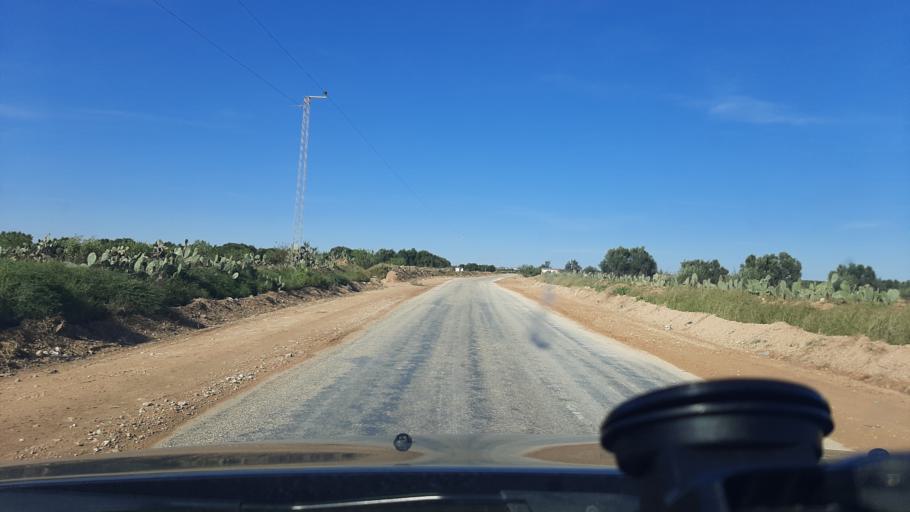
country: TN
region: Safaqis
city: Sfax
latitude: 34.9182
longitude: 10.5826
